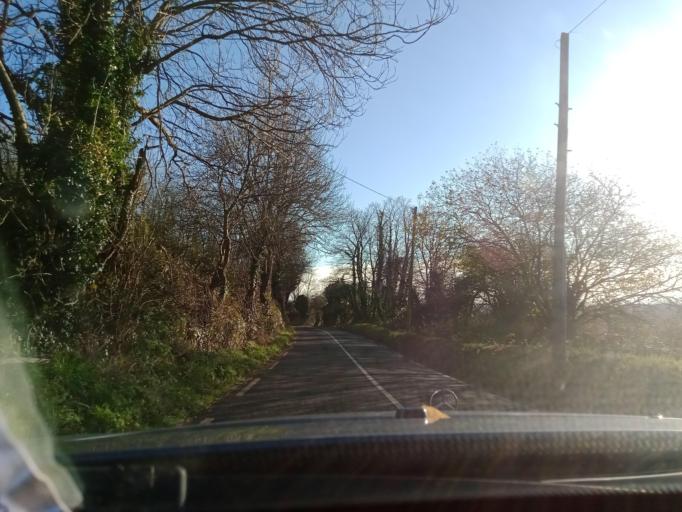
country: IE
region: Leinster
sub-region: Kilkenny
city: Piltown
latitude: 52.3983
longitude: -7.3777
